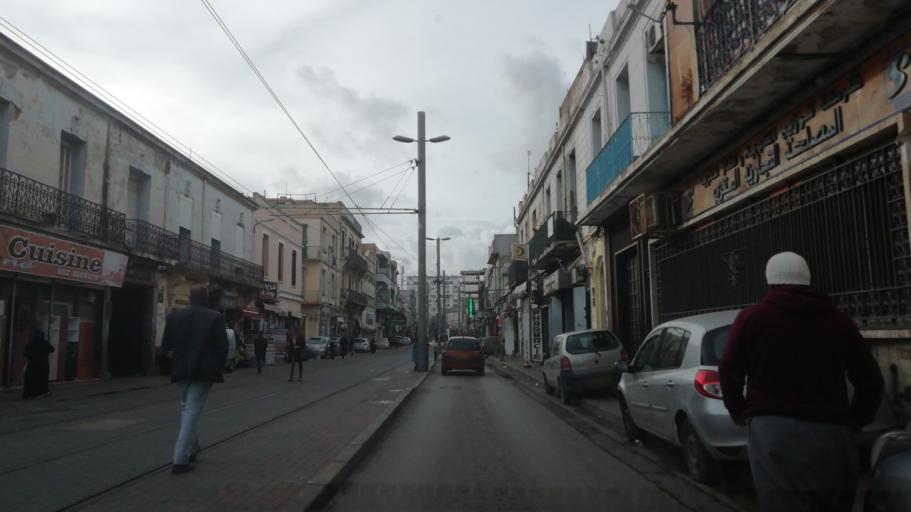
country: DZ
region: Oran
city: Oran
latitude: 35.6989
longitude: -0.6238
